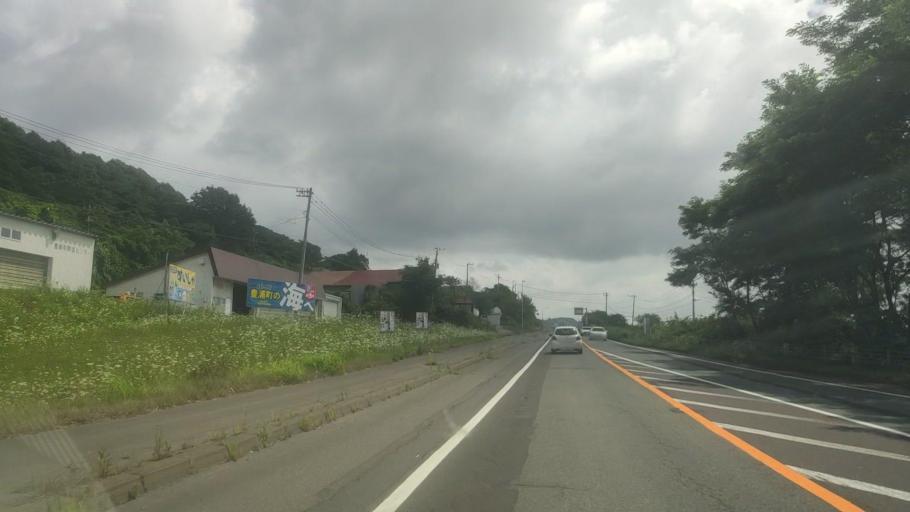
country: JP
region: Hokkaido
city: Niseko Town
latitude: 42.5888
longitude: 140.7060
